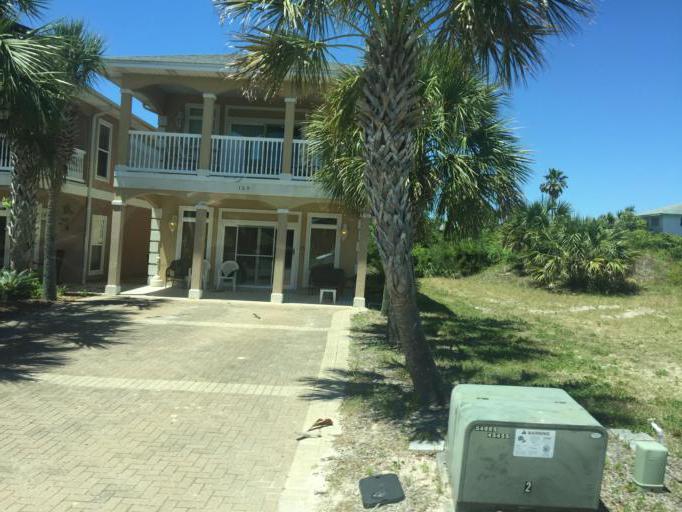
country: US
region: Florida
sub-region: Bay County
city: Laguna Beach
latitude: 30.2422
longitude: -85.9281
